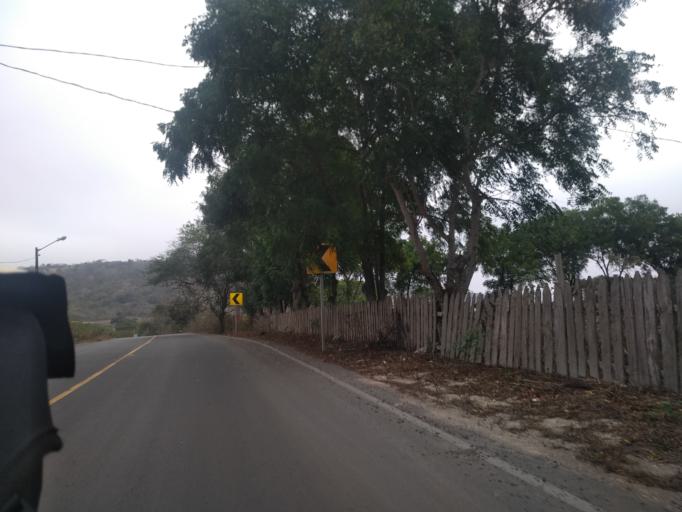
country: EC
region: Manabi
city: Montecristi
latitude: -1.0857
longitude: -80.6851
